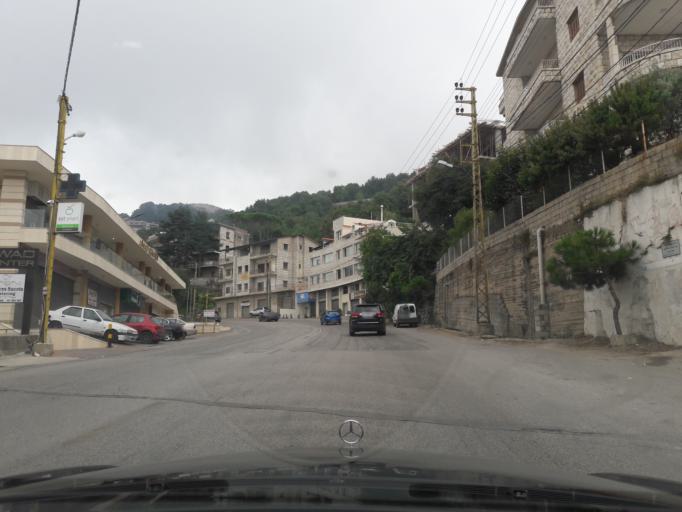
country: LB
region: Mont-Liban
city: Djounie
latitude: 33.9182
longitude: 35.6650
